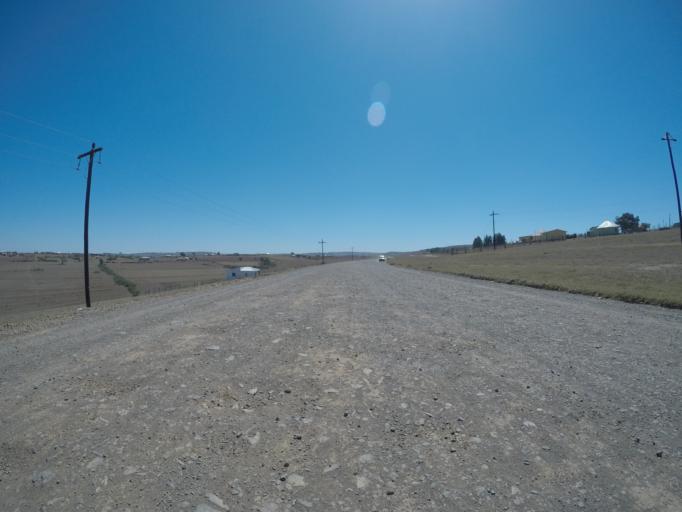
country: ZA
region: Eastern Cape
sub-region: OR Tambo District Municipality
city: Mthatha
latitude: -31.7867
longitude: 28.8126
